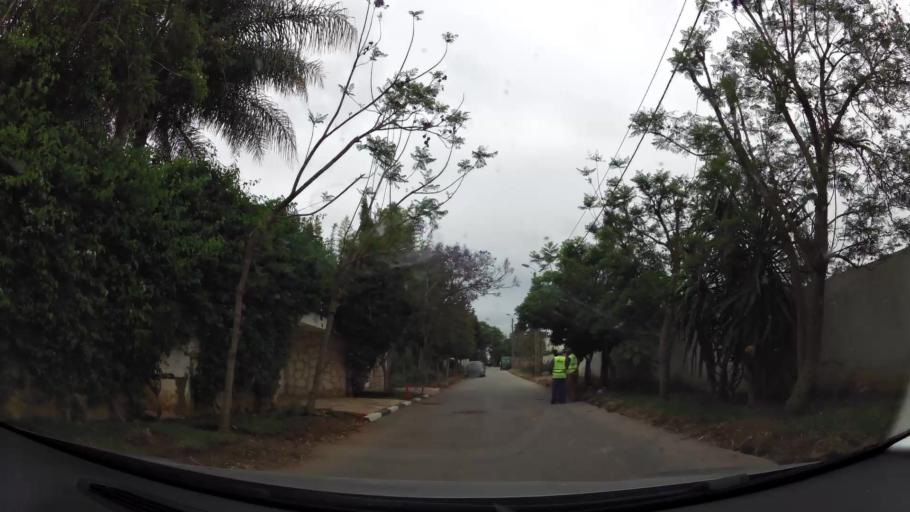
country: MA
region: Rabat-Sale-Zemmour-Zaer
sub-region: Rabat
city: Rabat
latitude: 33.9623
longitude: -6.8157
